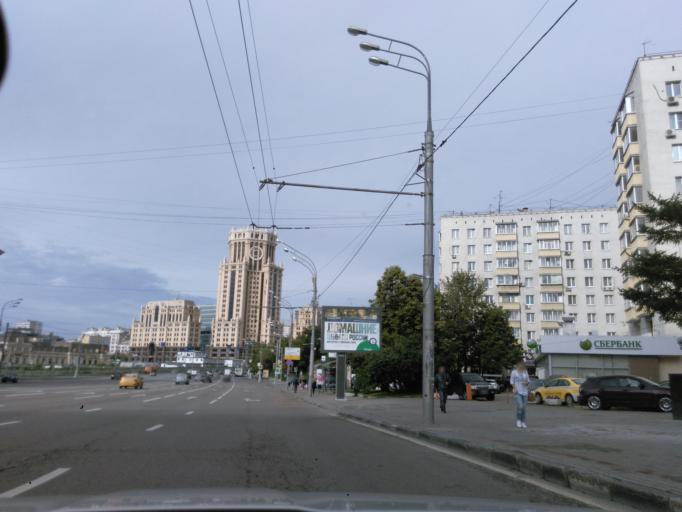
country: RU
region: Moscow
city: Zamoskvorech'ye
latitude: 55.7332
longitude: 37.6410
